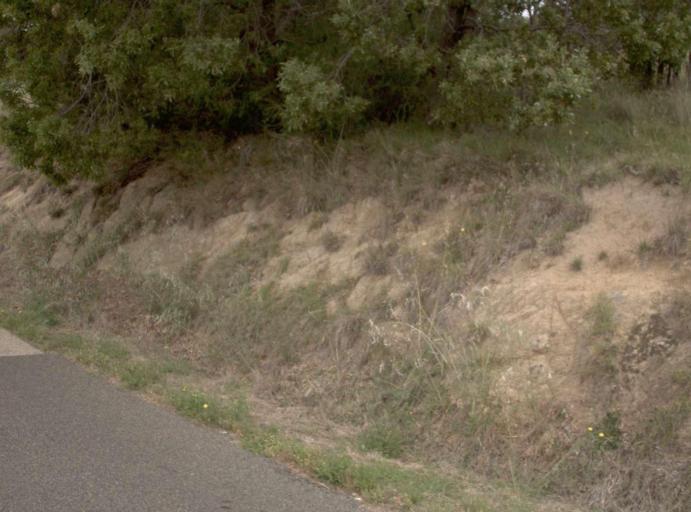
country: AU
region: Victoria
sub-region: East Gippsland
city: Bairnsdale
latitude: -37.4735
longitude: 147.2238
